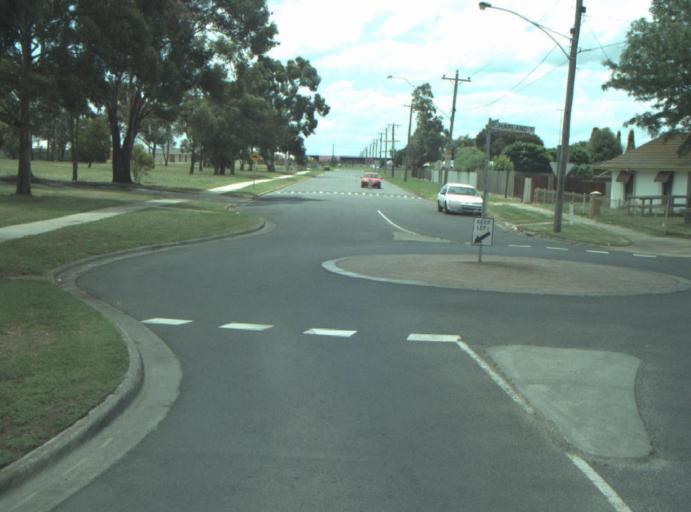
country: AU
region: Victoria
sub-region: Greater Geelong
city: Bell Park
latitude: -38.0655
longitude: 144.3678
